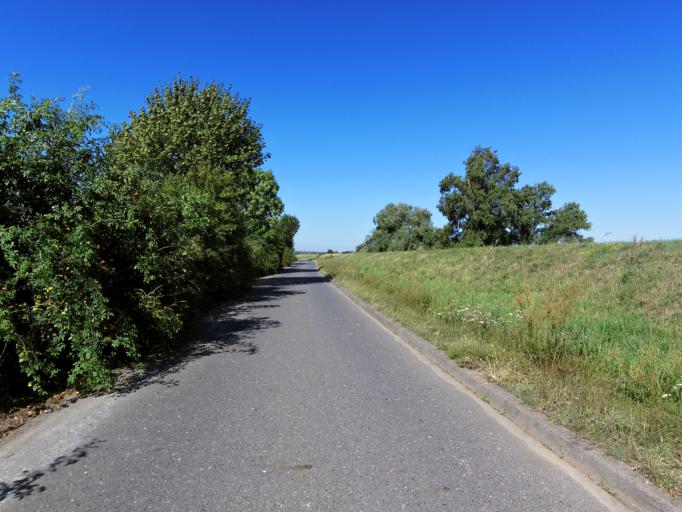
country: DE
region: Saxony-Anhalt
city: Prettin
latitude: 51.6445
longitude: 12.9062
